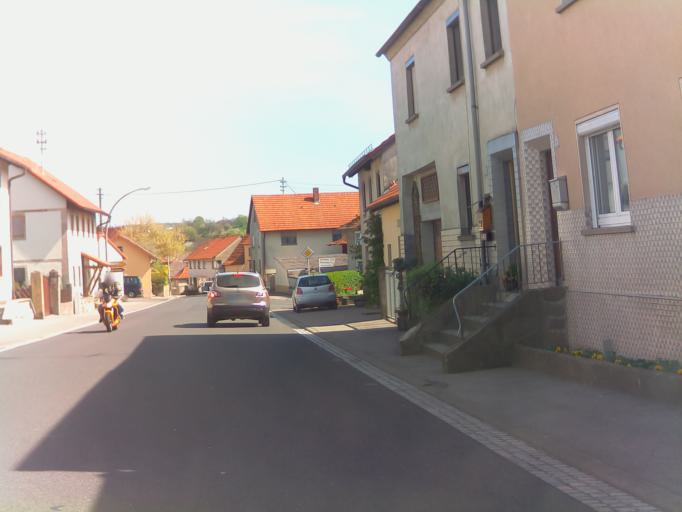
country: DE
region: Bavaria
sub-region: Regierungsbezirk Unterfranken
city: Ermershausen
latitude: 50.2098
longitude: 10.6221
